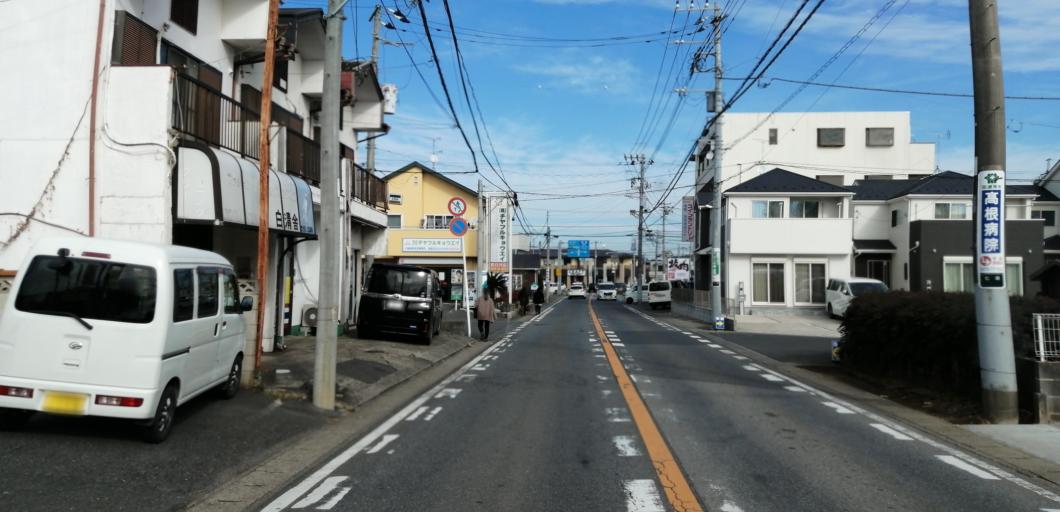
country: JP
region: Chiba
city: Narita
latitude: 35.7384
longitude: 140.3213
